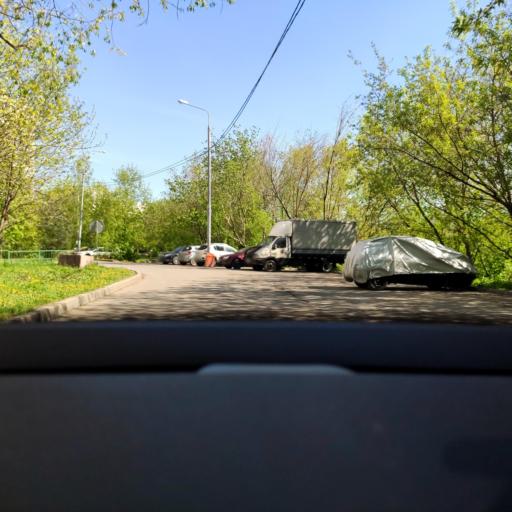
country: RU
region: Moscow
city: Kozeyevo
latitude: 55.8732
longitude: 37.6201
